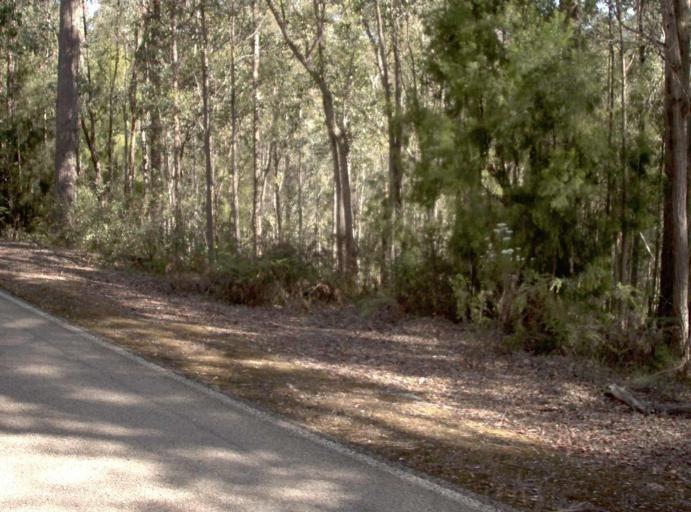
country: AU
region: Victoria
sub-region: East Gippsland
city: Lakes Entrance
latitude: -37.5624
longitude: 148.5572
